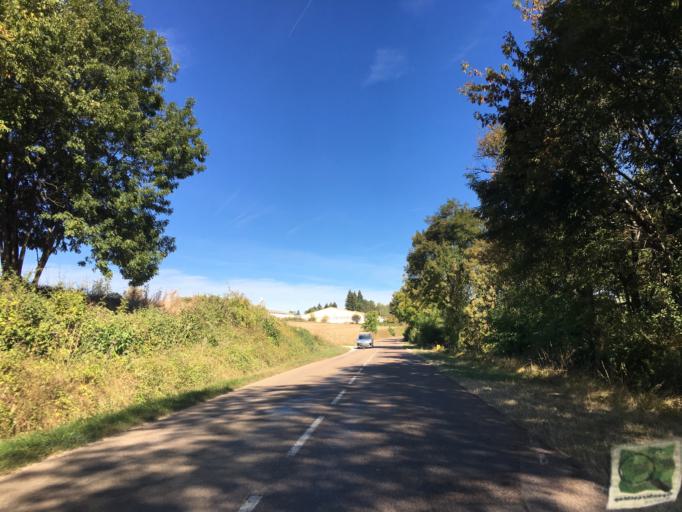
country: FR
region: Bourgogne
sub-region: Departement de l'Yonne
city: Vermenton
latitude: 47.6521
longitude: 3.6589
